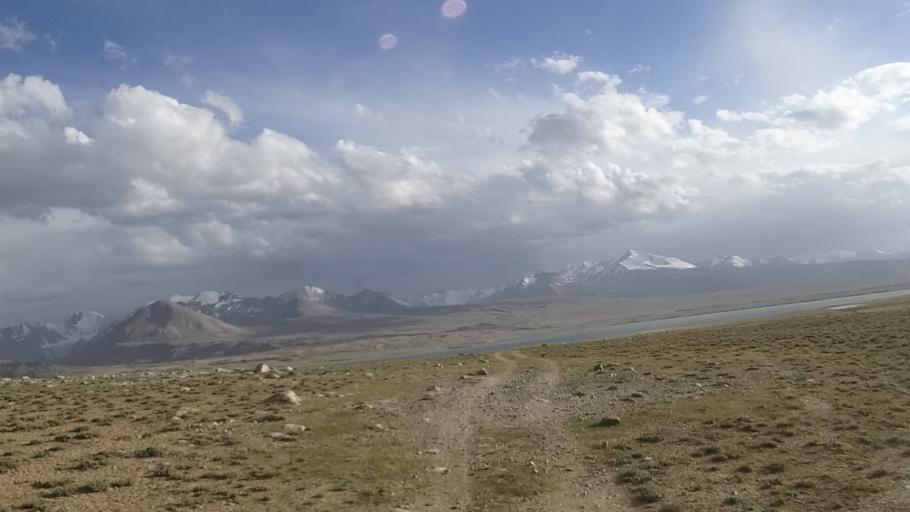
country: TJ
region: Gorno-Badakhshan
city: Murghob
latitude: 37.4659
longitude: 73.6136
